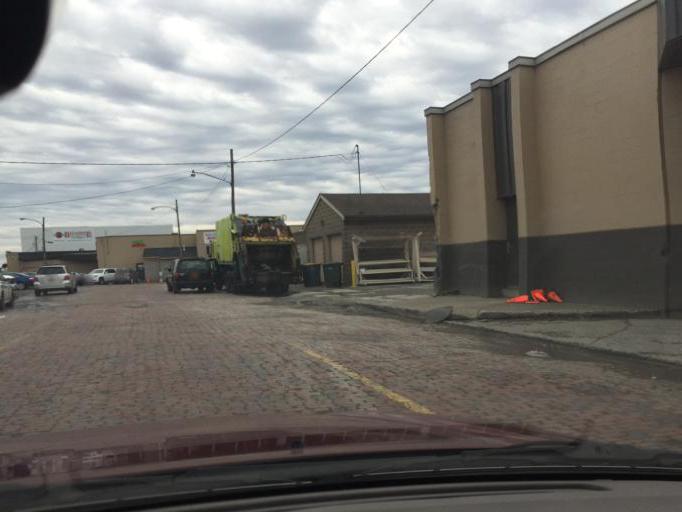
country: US
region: New York
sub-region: Monroe County
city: Rochester
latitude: 43.1648
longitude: -77.5896
